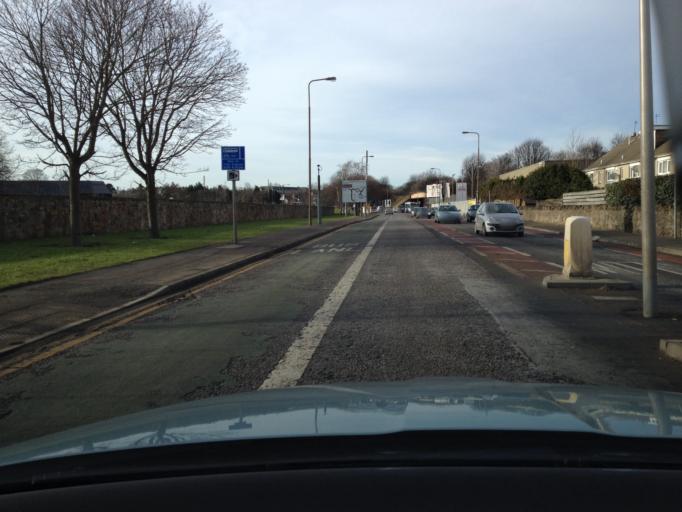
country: GB
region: Scotland
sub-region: West Lothian
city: Seafield
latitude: 55.9277
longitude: -3.1575
